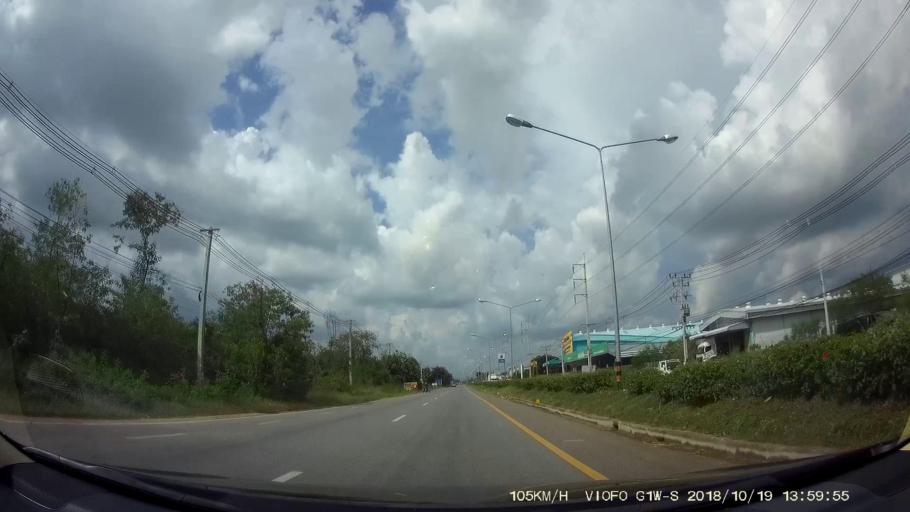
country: TH
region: Chaiyaphum
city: Chaiyaphum
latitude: 15.8170
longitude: 102.0601
